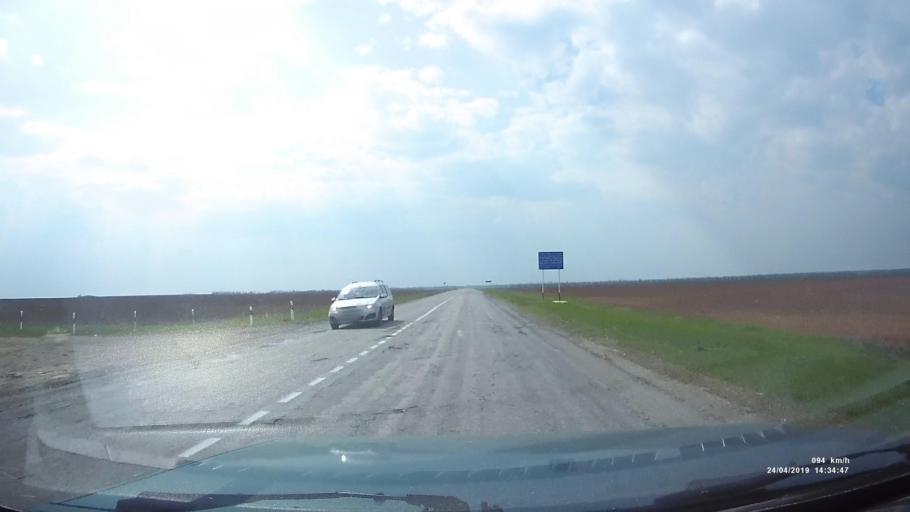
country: RU
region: Kalmykiya
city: Arshan'
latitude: 46.3738
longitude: 43.9245
